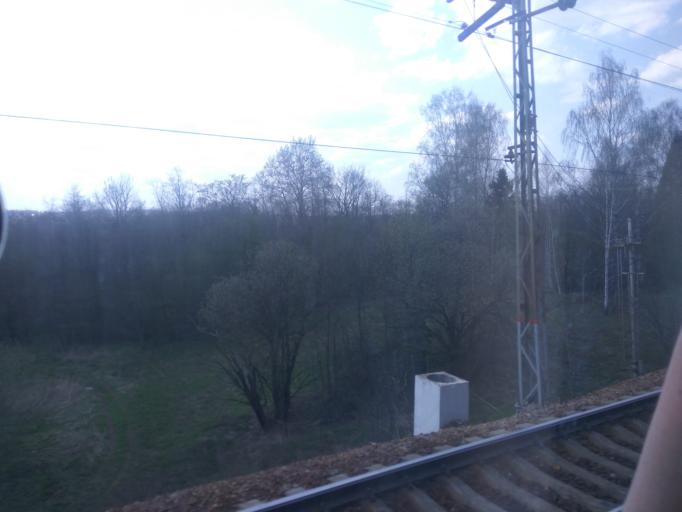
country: RU
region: Moskovskaya
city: Dedenevo
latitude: 56.2677
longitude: 37.5093
